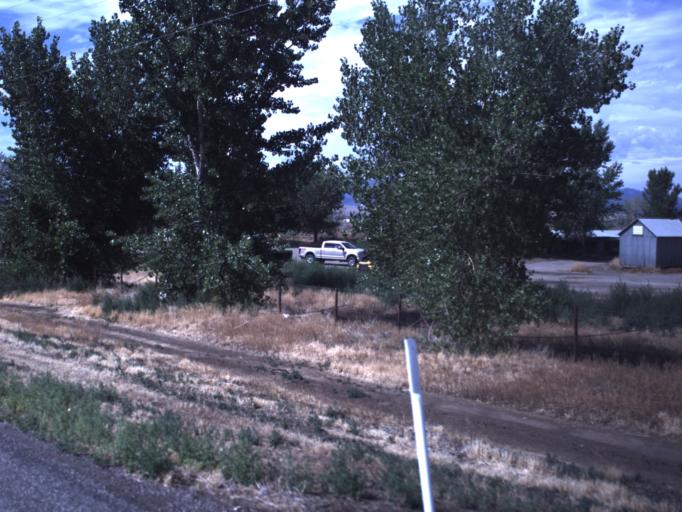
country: US
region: Utah
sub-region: Sevier County
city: Monroe
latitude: 38.6783
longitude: -112.1214
